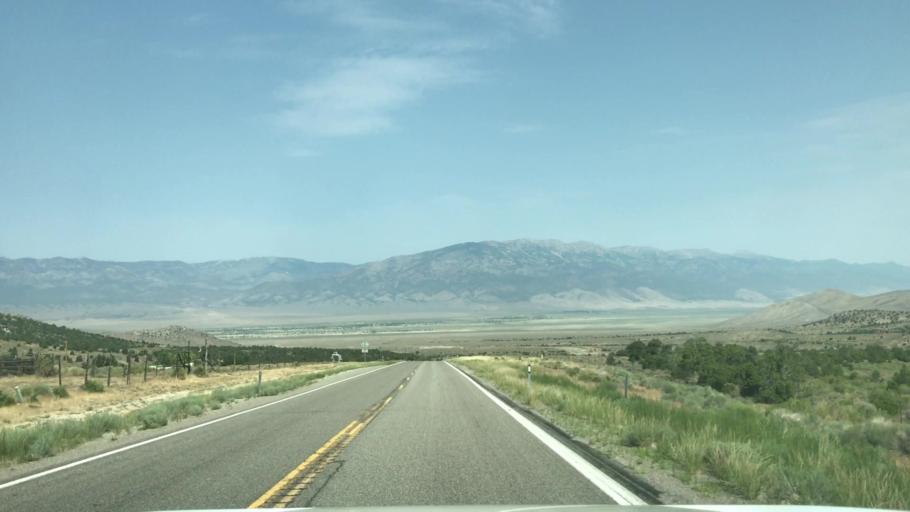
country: US
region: Nevada
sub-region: White Pine County
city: McGill
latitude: 39.1636
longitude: -114.3594
